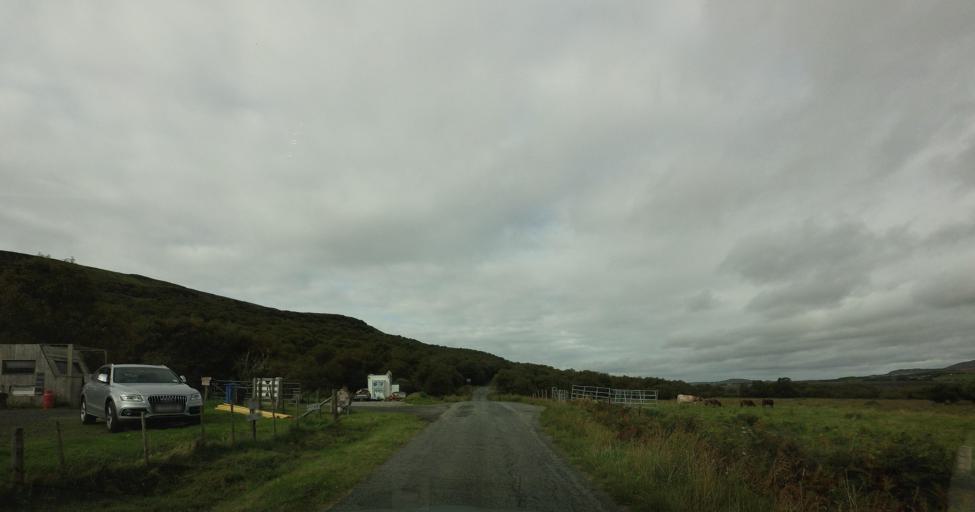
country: GB
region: Scotland
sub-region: Highland
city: Portree
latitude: 57.4178
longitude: -6.2341
